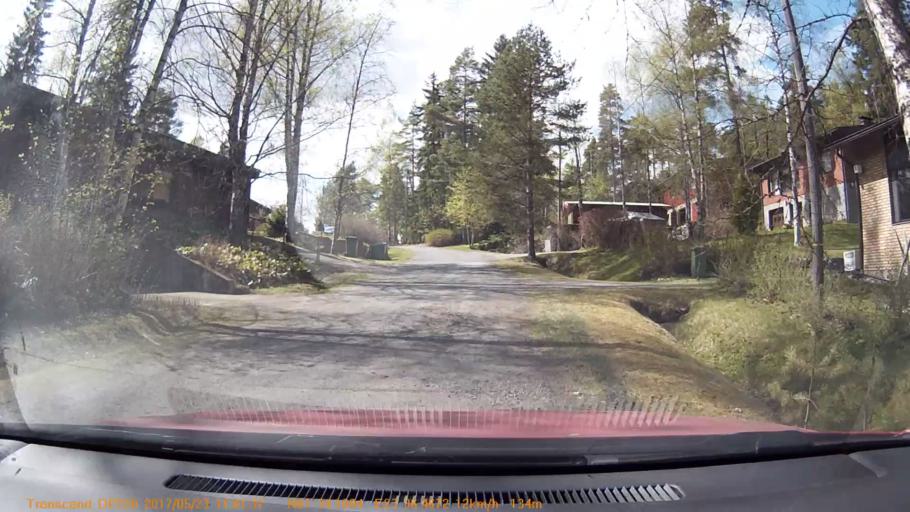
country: FI
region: Pirkanmaa
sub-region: Tampere
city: Yloejaervi
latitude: 61.5698
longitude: 23.6079
